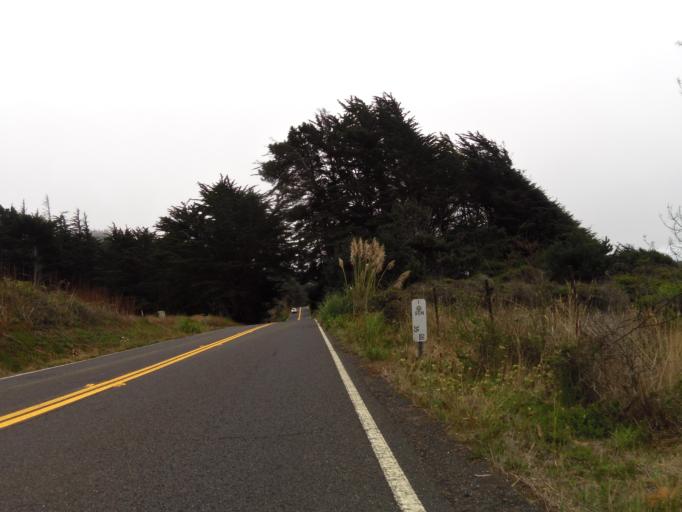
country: US
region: California
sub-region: Sonoma County
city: Sea Ranch
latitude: 38.5300
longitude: -123.2672
